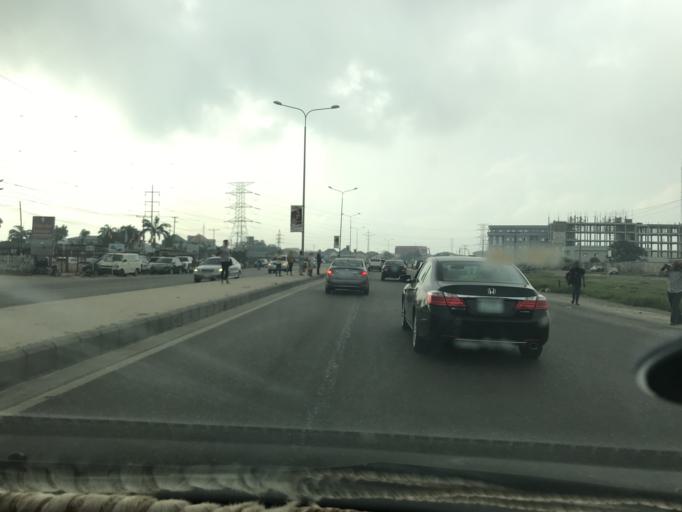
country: NG
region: Lagos
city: Ikoyi
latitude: 6.4553
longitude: 3.5550
